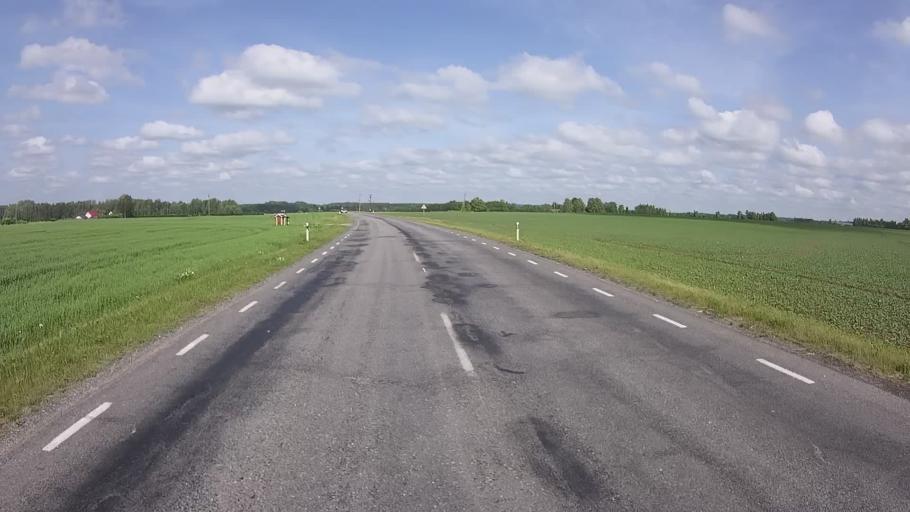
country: EE
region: Vorumaa
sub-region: Antsla vald
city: Vana-Antsla
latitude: 57.9005
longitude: 26.4768
